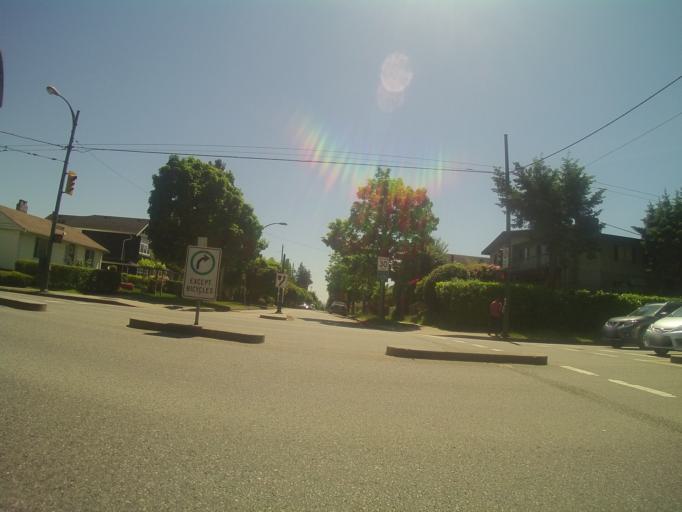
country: CA
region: British Columbia
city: Vancouver
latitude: 49.2332
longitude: -123.1057
